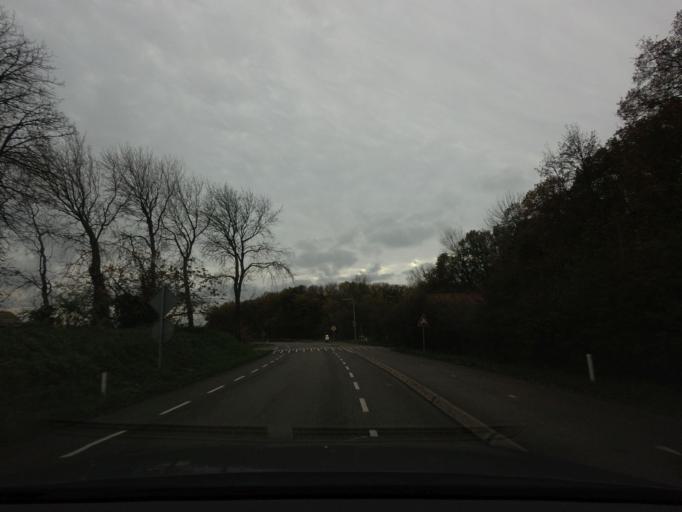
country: NL
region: North Holland
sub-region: Gemeente Bergen
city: Egmond aan Zee
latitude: 52.6402
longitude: 4.6576
